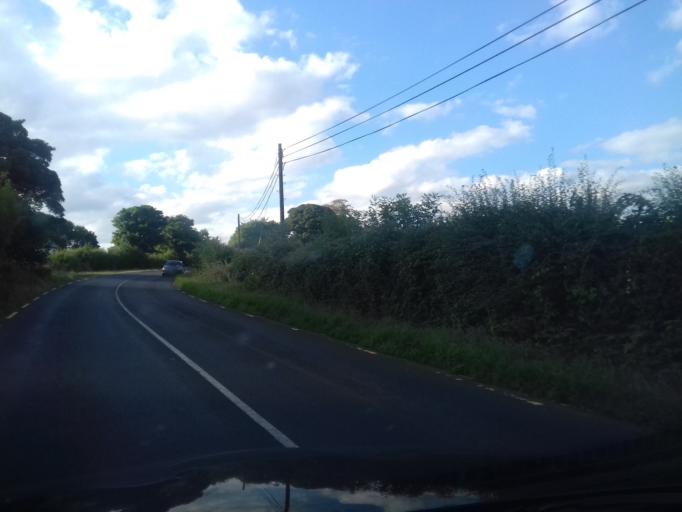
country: IE
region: Leinster
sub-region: Loch Garman
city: New Ross
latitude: 52.4447
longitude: -6.9623
